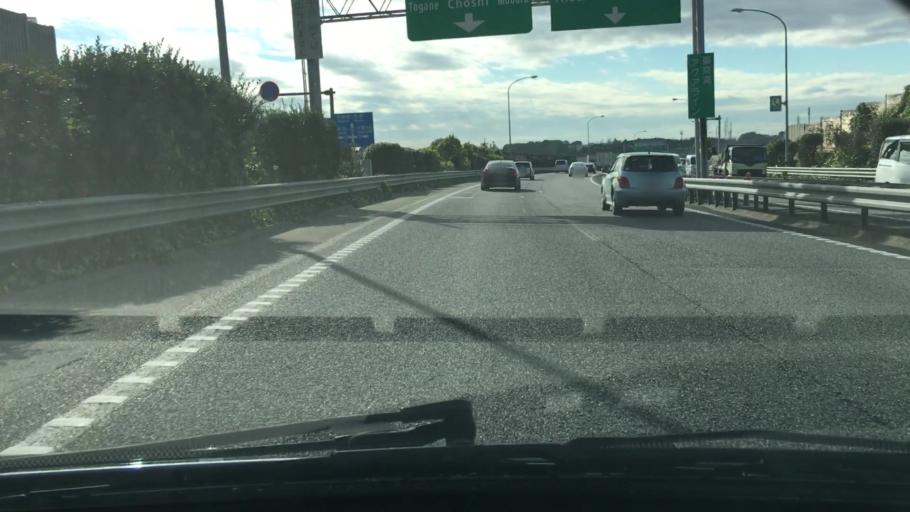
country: JP
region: Chiba
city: Chiba
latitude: 35.6116
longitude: 140.1532
